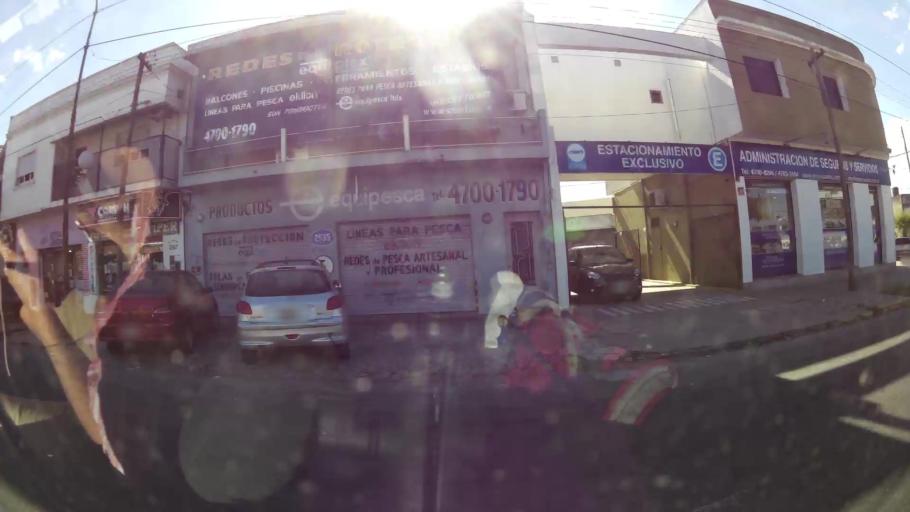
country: AR
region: Buenos Aires
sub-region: Partido de General San Martin
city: General San Martin
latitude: -34.5141
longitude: -58.5680
